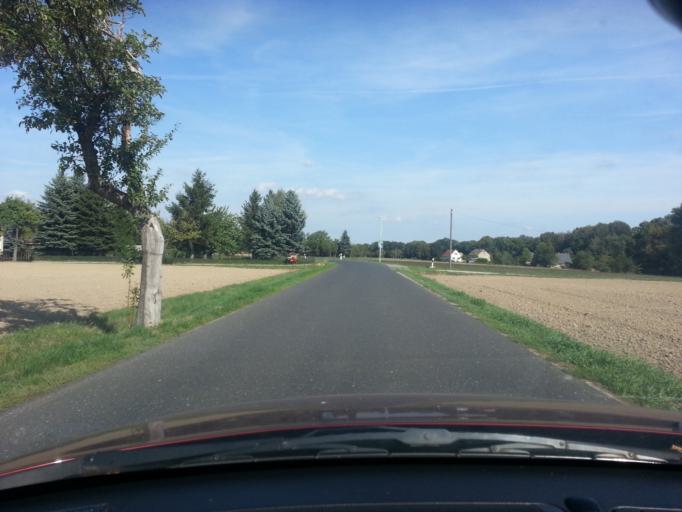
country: DE
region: Saxony
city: Reichenbach
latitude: 51.1096
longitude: 14.8324
